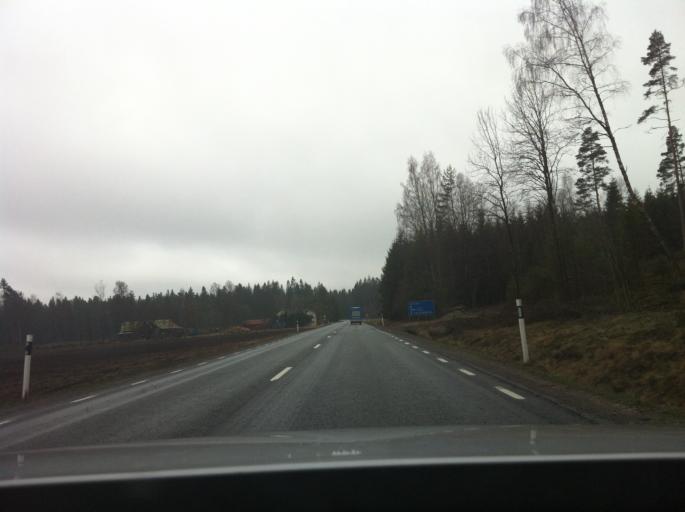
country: SE
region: Vaestra Goetaland
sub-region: Svenljunga Kommun
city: Svenljunga
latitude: 57.4350
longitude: 13.0935
